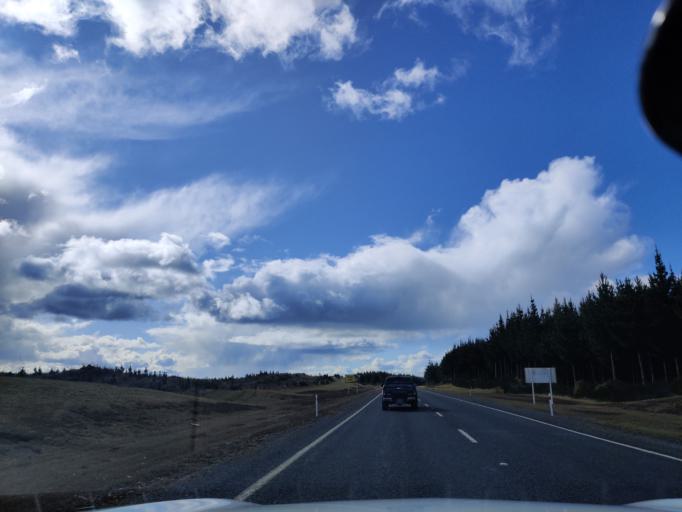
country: NZ
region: Waikato
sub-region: Taupo District
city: Taupo
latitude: -38.8350
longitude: 176.0651
